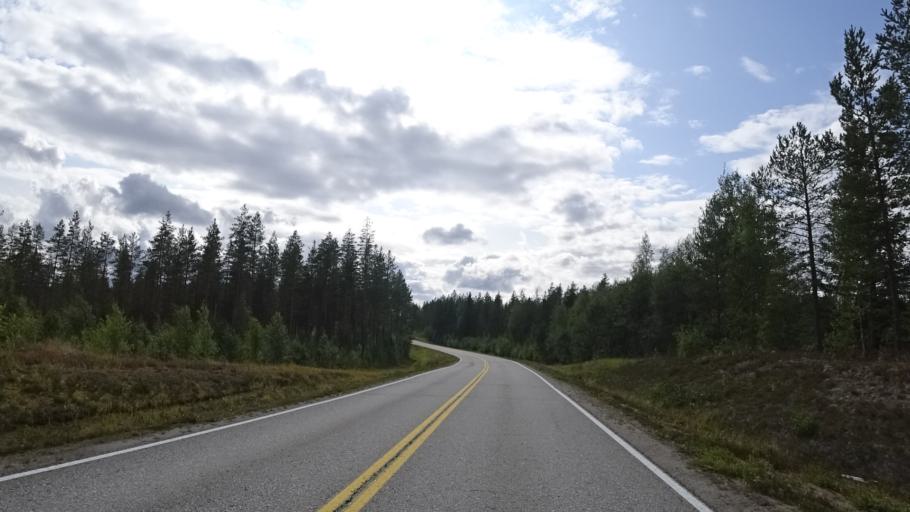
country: FI
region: North Karelia
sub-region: Joensuu
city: Ilomantsi
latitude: 62.7923
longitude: 31.1014
